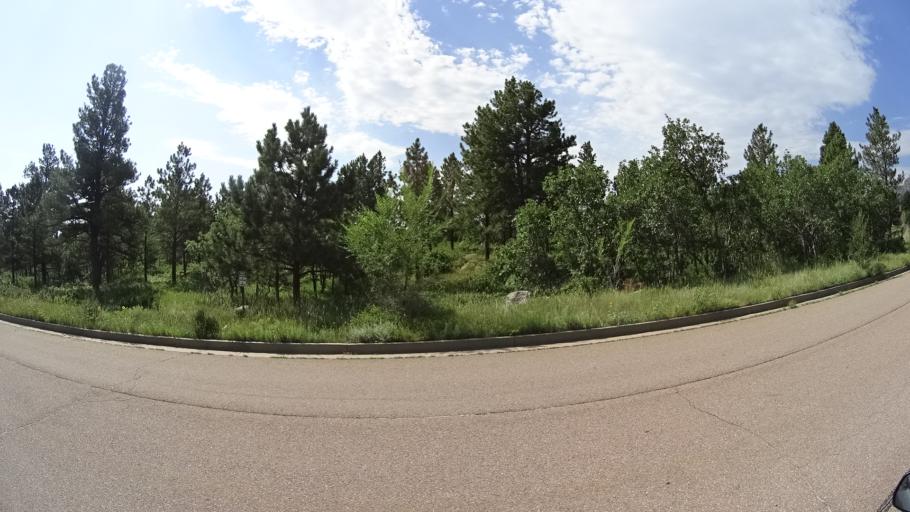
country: US
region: Colorado
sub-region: El Paso County
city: Fort Carson
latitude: 38.7467
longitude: -104.8295
